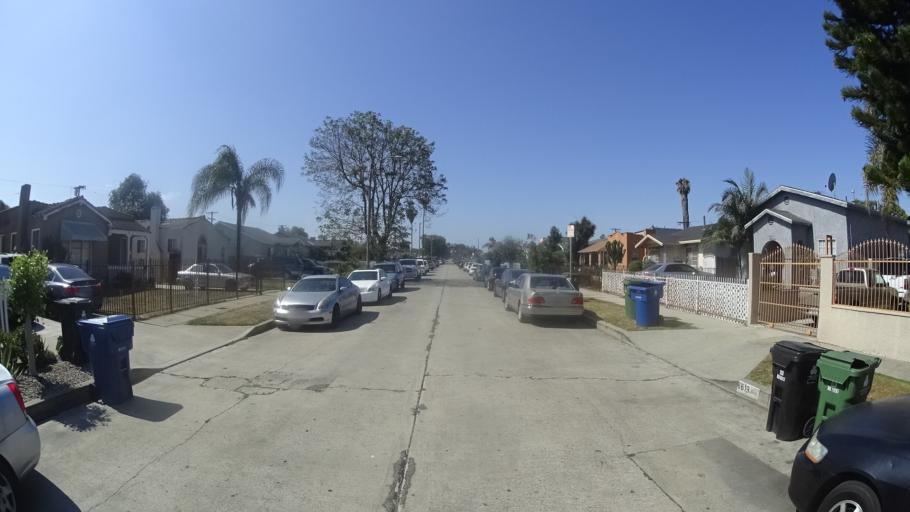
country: US
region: California
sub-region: Los Angeles County
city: View Park-Windsor Hills
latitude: 33.9796
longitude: -118.3235
